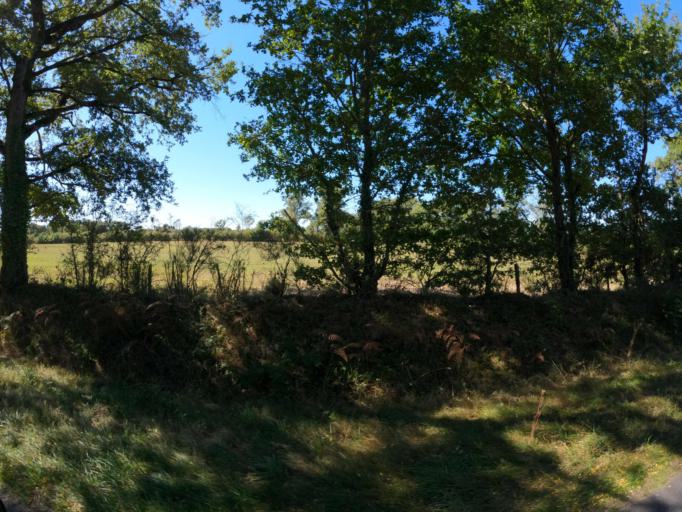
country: FR
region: Poitou-Charentes
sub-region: Departement de la Vienne
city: Lathus-Saint-Remy
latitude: 46.3113
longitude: 0.9800
